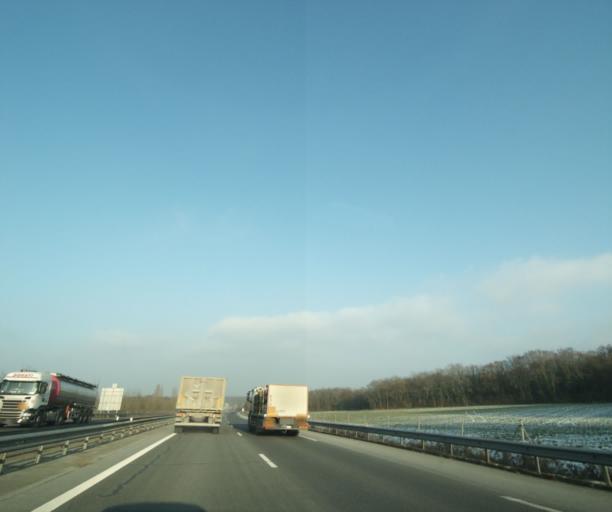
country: FR
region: Rhone-Alpes
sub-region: Departement de la Haute-Savoie
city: Valleiry
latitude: 46.1035
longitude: 5.9770
